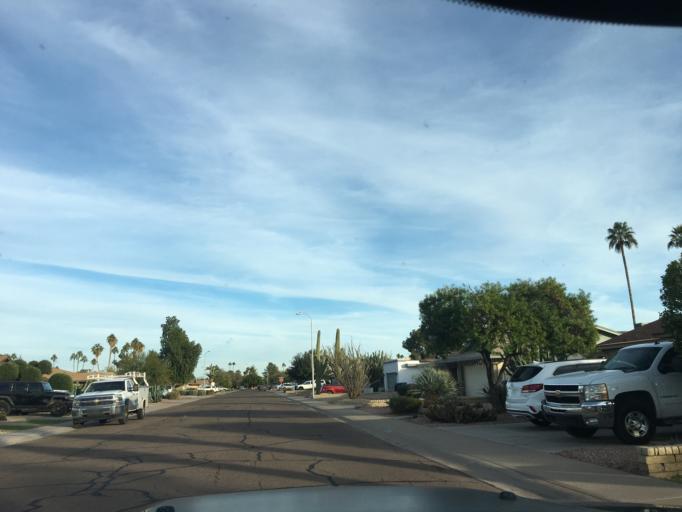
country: US
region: Arizona
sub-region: Maricopa County
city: Tempe
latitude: 33.3732
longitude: -111.9093
